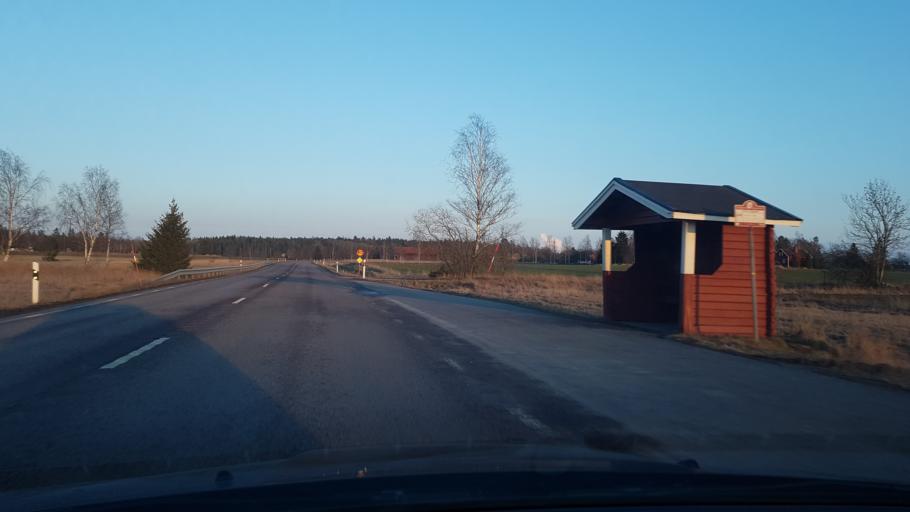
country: SE
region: Uppsala
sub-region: Enkopings Kommun
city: Orsundsbro
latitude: 59.8787
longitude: 17.2704
